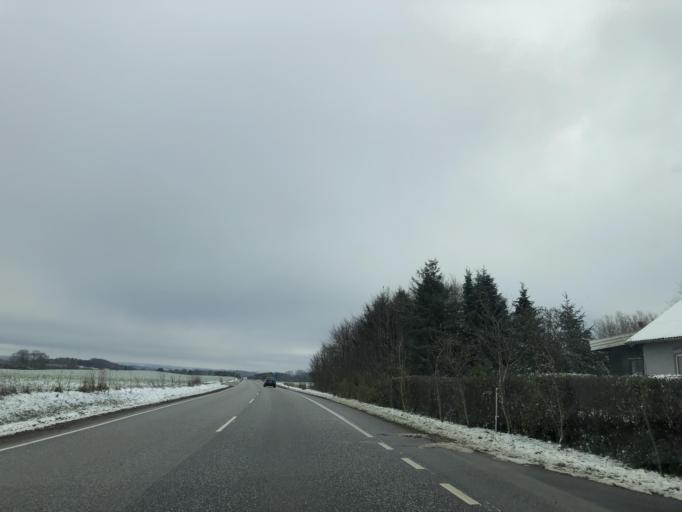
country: DK
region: Central Jutland
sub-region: Hedensted Kommune
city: Hedensted
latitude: 55.8954
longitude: 9.7253
